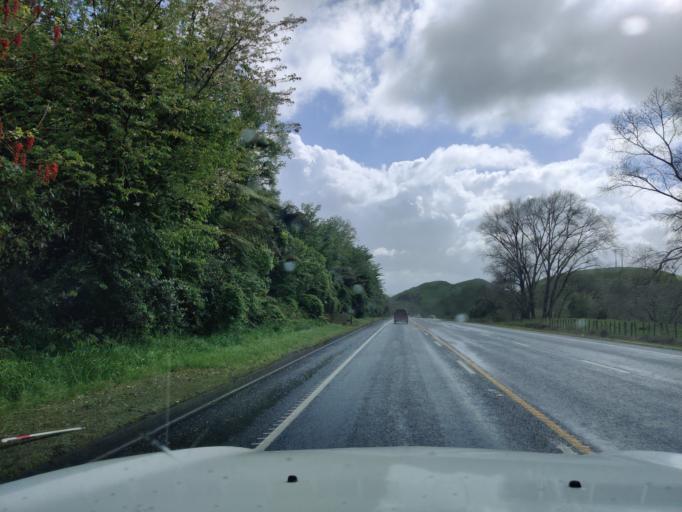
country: NZ
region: Waikato
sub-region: Matamata-Piako District
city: Matamata
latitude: -37.9792
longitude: 175.7387
